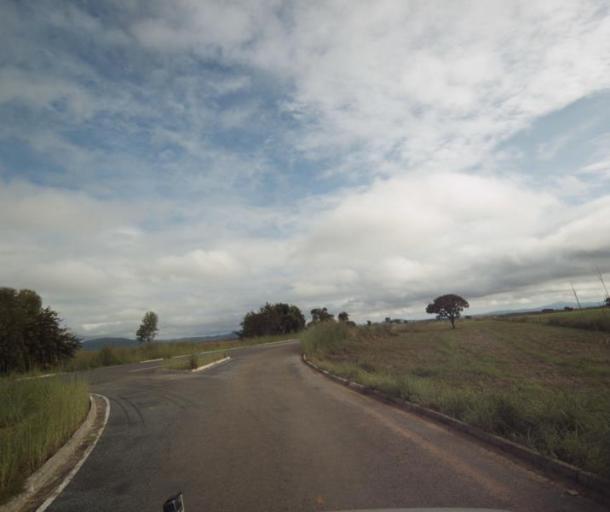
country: BR
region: Goias
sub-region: Padre Bernardo
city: Padre Bernardo
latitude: -15.3573
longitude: -48.6463
